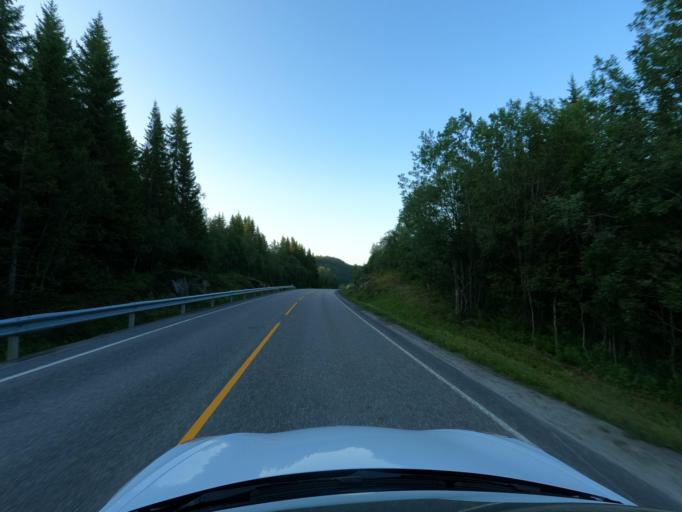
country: NO
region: Troms
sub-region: Harstad
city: Harstad
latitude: 68.7249
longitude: 16.5374
